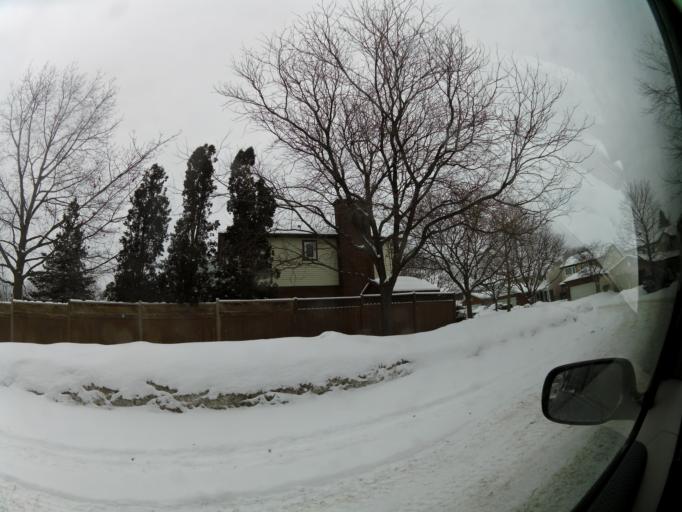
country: CA
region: Ontario
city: Ottawa
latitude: 45.3740
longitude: -75.6161
